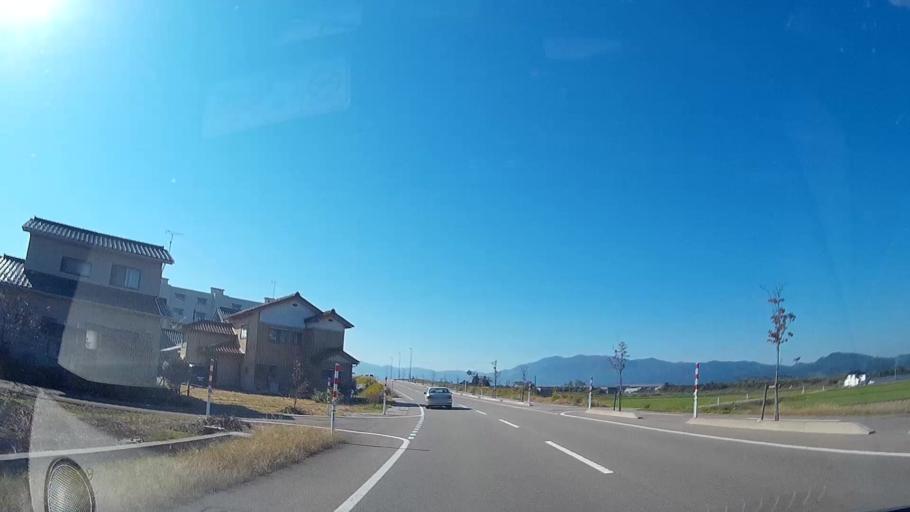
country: JP
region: Toyama
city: Nanto-shi
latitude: 36.5836
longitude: 136.9083
